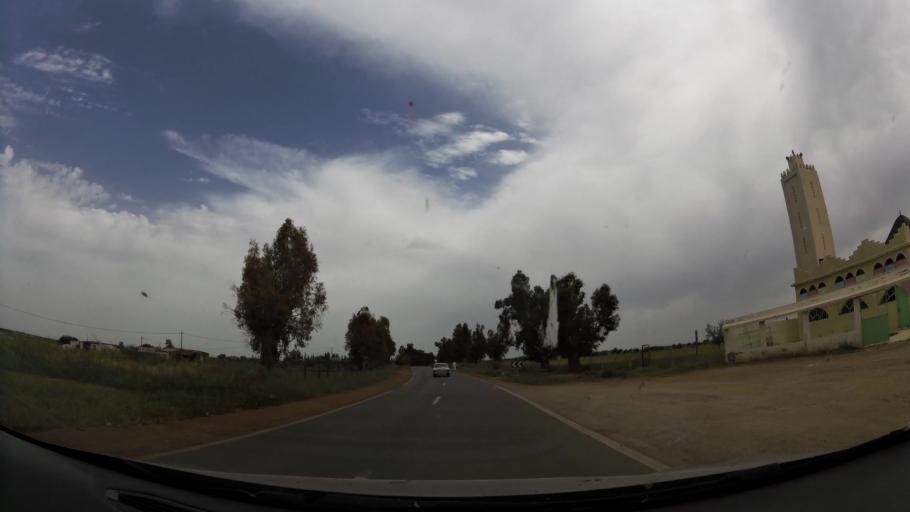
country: MA
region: Rabat-Sale-Zemmour-Zaer
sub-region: Khemisset
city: Tiflet
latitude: 33.8352
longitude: -6.2720
